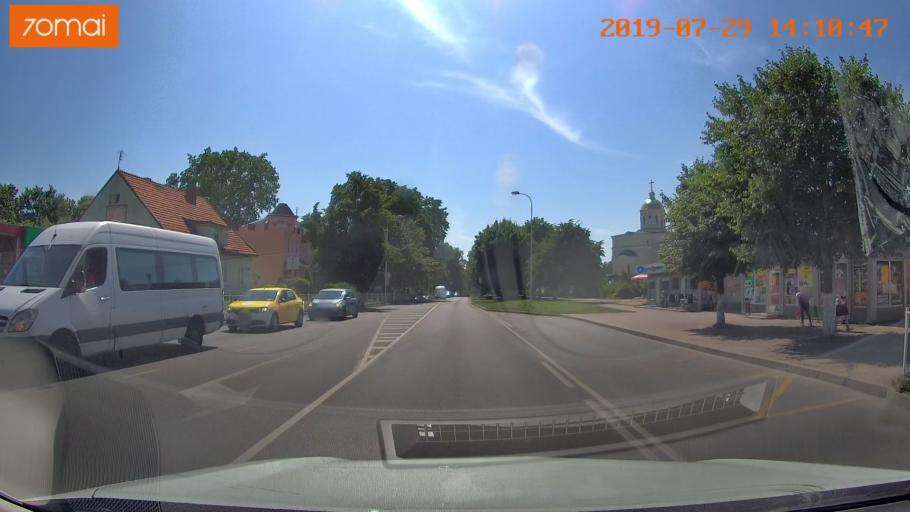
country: RU
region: Kaliningrad
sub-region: Gorod Kaliningrad
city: Baltiysk
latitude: 54.6543
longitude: 19.9115
